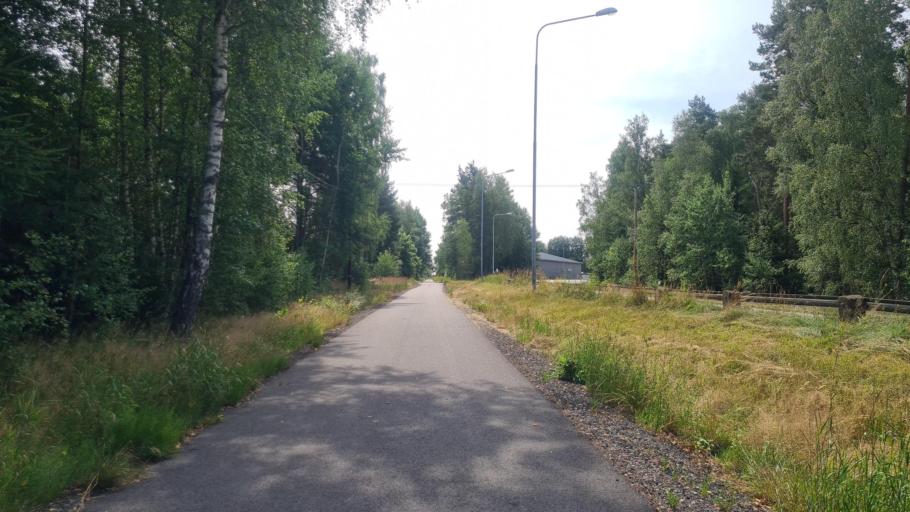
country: SE
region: Kronoberg
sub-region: Ljungby Kommun
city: Lagan
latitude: 56.9096
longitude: 13.9899
